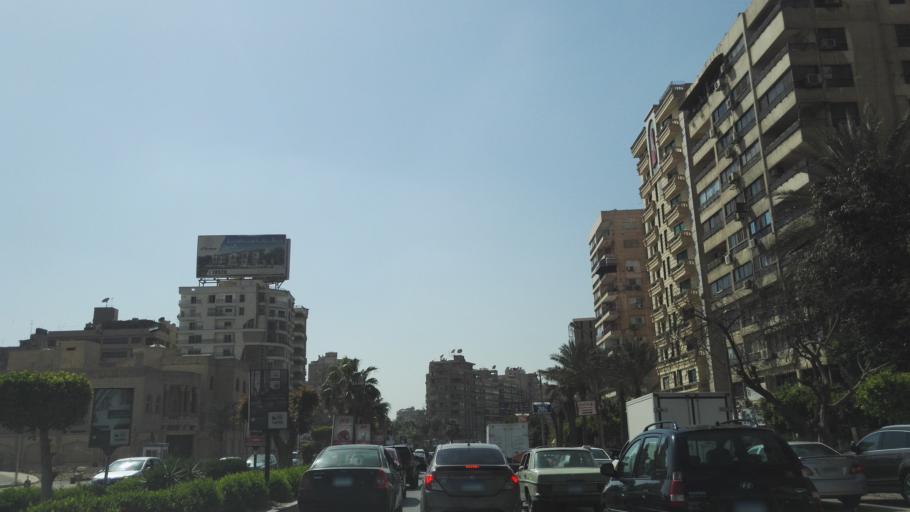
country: EG
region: Muhafazat al Qahirah
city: Cairo
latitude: 30.0816
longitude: 31.3467
